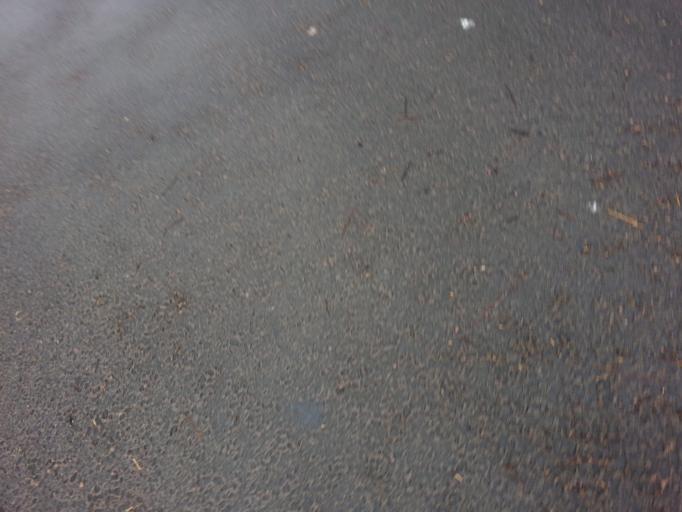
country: NO
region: Oslo
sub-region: Oslo
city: Oslo
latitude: 59.9176
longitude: 10.7267
